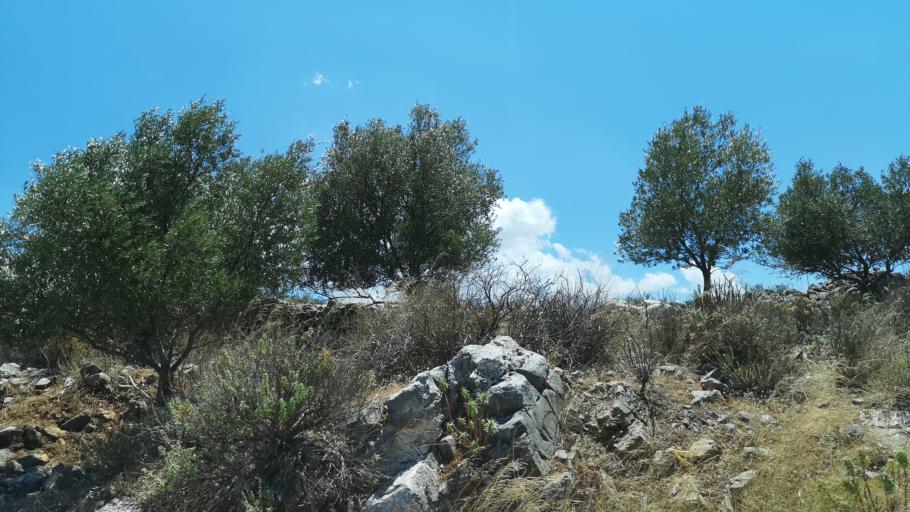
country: GR
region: Crete
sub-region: Nomos Lasithiou
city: Neapoli
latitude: 35.2535
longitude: 25.6333
